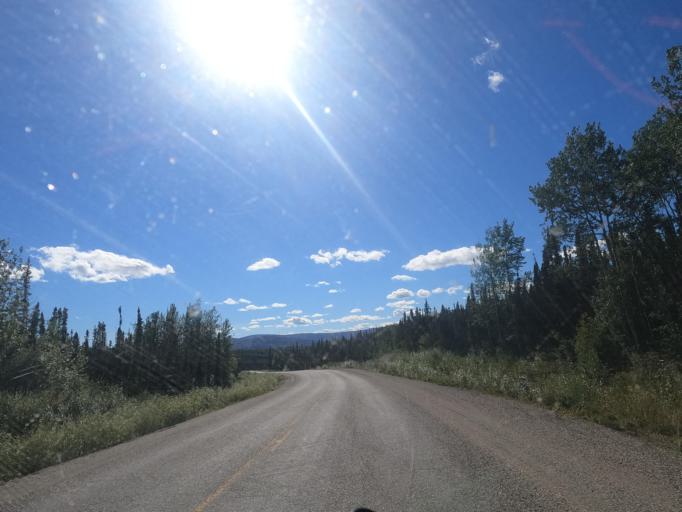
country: CA
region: Yukon
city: Dawson City
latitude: 63.9379
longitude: -138.4844
